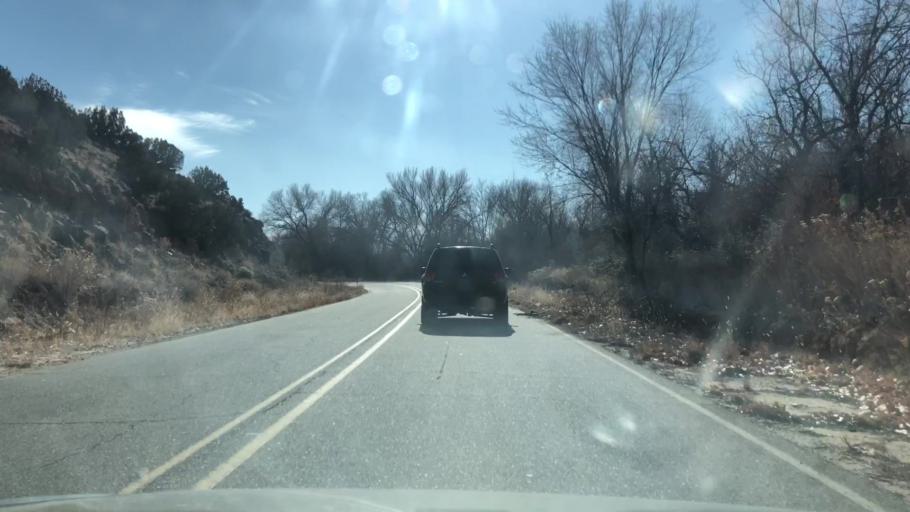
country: US
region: New Mexico
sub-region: Rio Arriba County
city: Ohkay Owingeh
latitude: 36.0894
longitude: -106.1294
